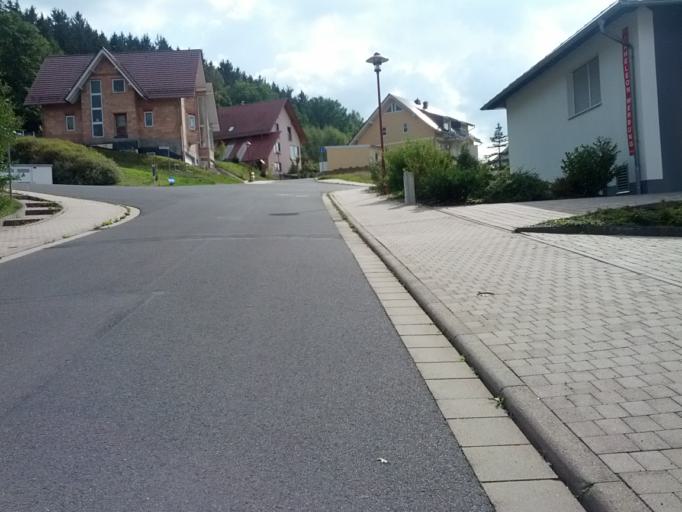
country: DE
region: Thuringia
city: Thal
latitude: 50.9453
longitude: 10.3978
